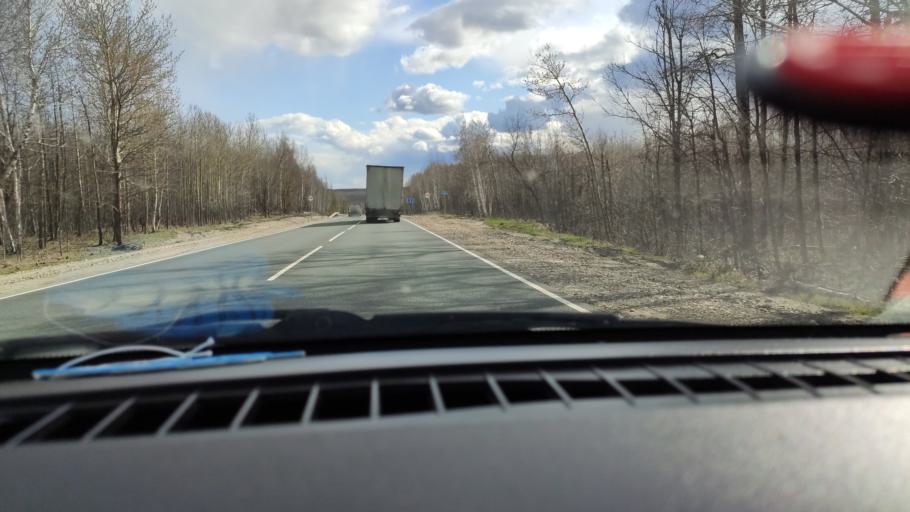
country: RU
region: Saratov
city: Alekseyevka
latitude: 52.4172
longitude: 48.0078
